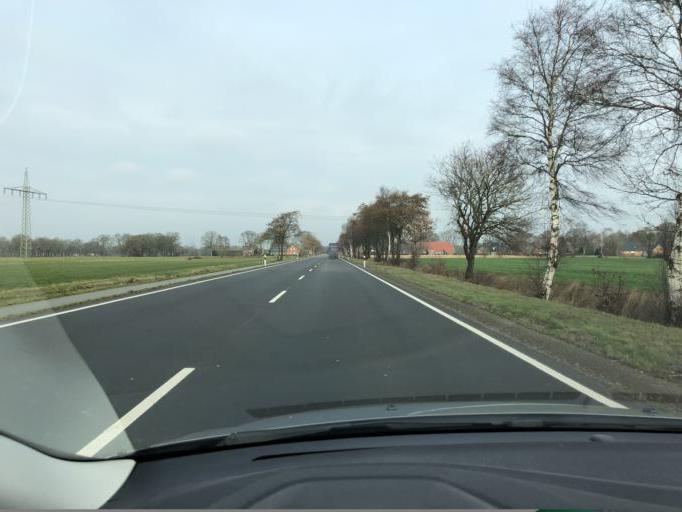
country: DE
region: Lower Saxony
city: Mittegrossefehn
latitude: 53.3787
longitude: 7.5826
